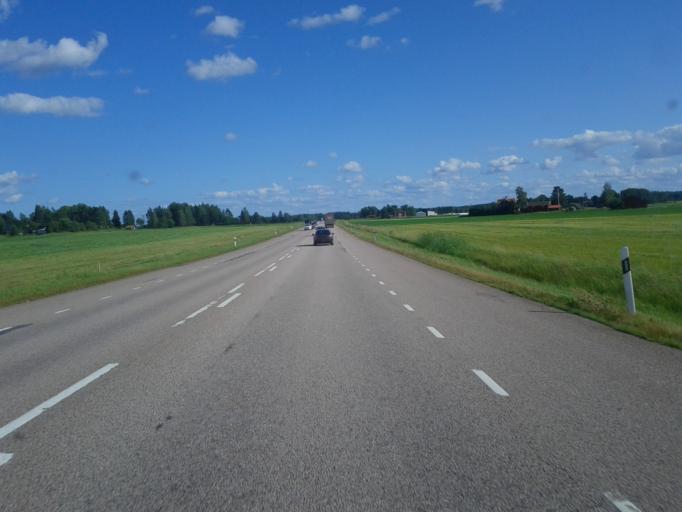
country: SE
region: Uppsala
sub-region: Enkopings Kommun
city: Enkoping
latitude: 59.6926
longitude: 17.0285
